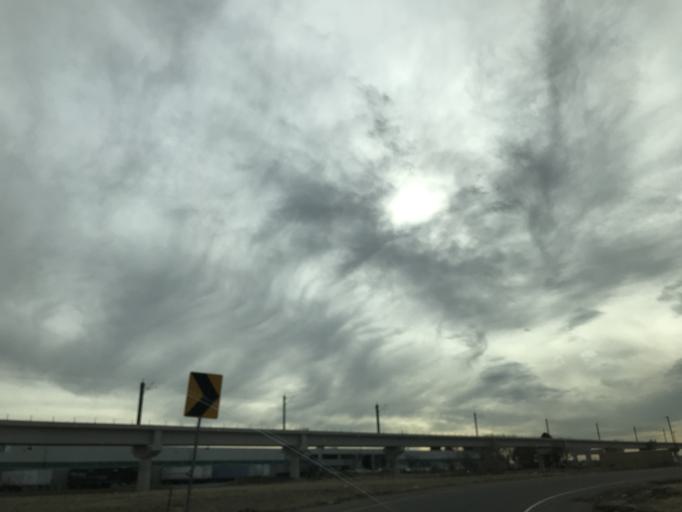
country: US
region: Colorado
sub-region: Adams County
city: Aurora
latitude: 39.7646
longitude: -104.7891
